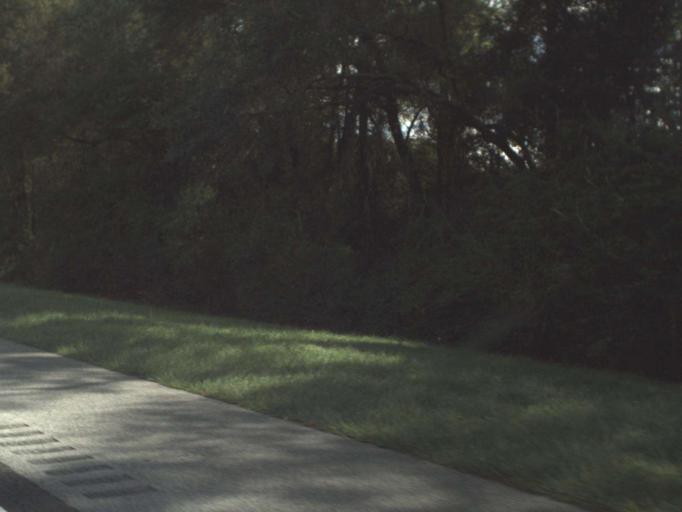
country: US
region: Florida
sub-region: Jackson County
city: Sneads
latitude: 30.6764
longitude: -85.0786
